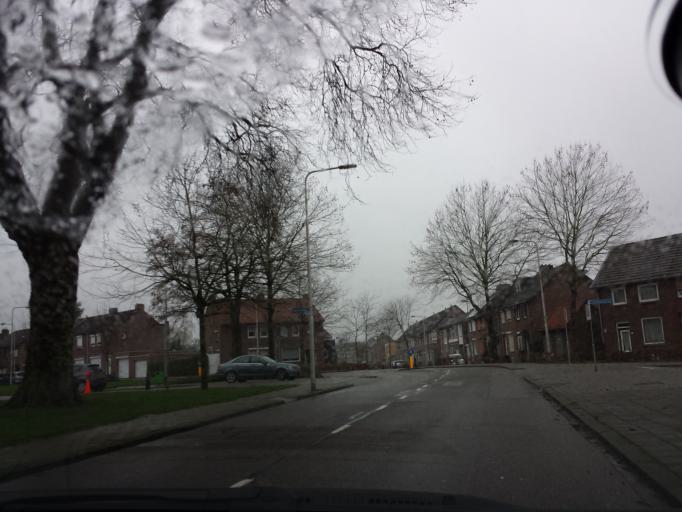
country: NL
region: Limburg
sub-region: Gemeente Kerkrade
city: Kerkrade
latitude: 50.8779
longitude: 6.0710
